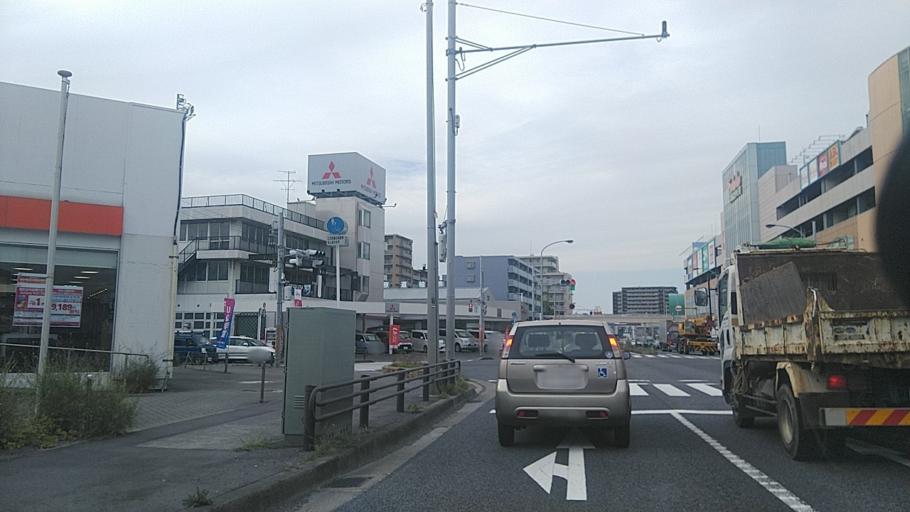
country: JP
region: Chiba
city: Yotsukaido
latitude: 35.7202
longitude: 140.1164
